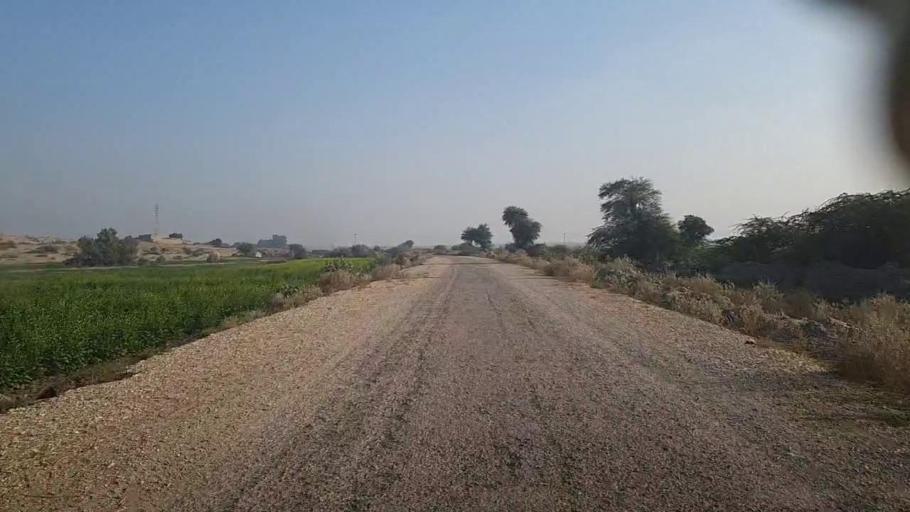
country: PK
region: Sindh
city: Karaundi
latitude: 26.7239
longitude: 68.4900
